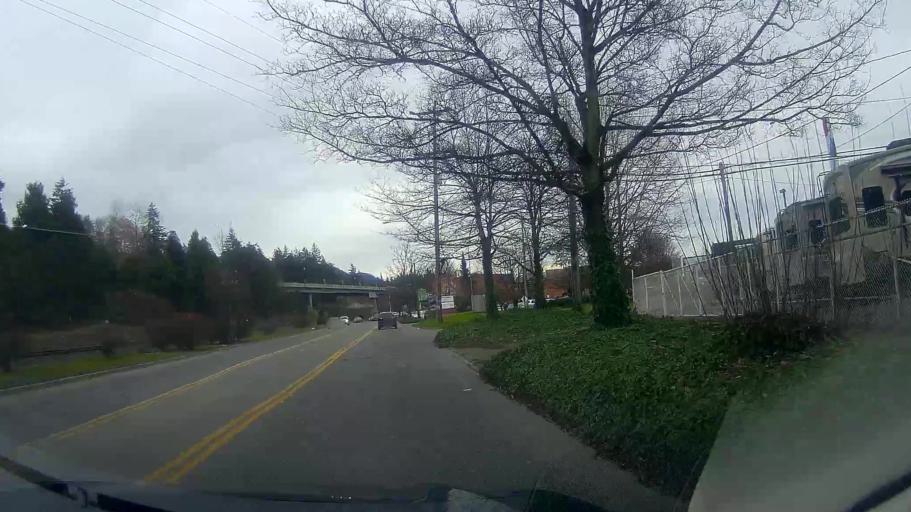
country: US
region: Washington
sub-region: Skagit County
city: Mount Vernon
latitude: 48.4235
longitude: -122.3373
